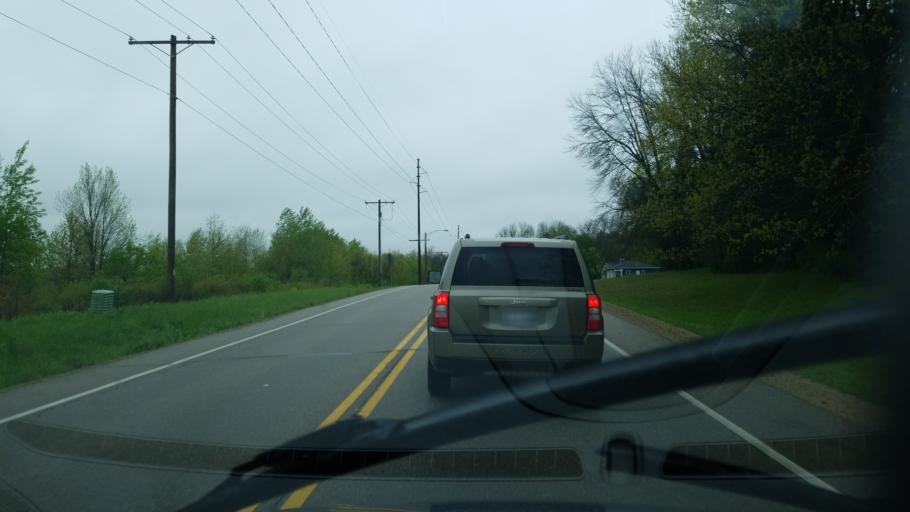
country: US
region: Wisconsin
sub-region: Dane County
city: Fitchburg
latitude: 42.9775
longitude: -89.4303
